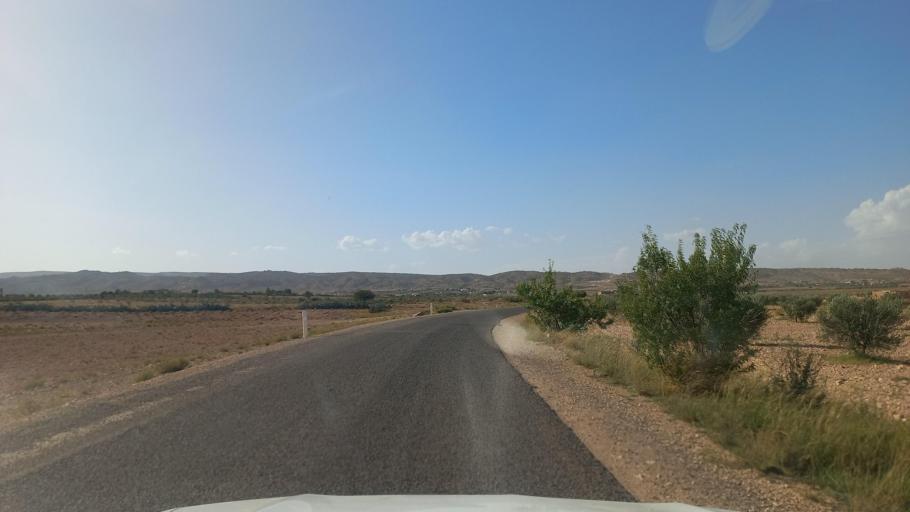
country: TN
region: Al Qasrayn
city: Sbiba
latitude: 35.3354
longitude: 9.0014
